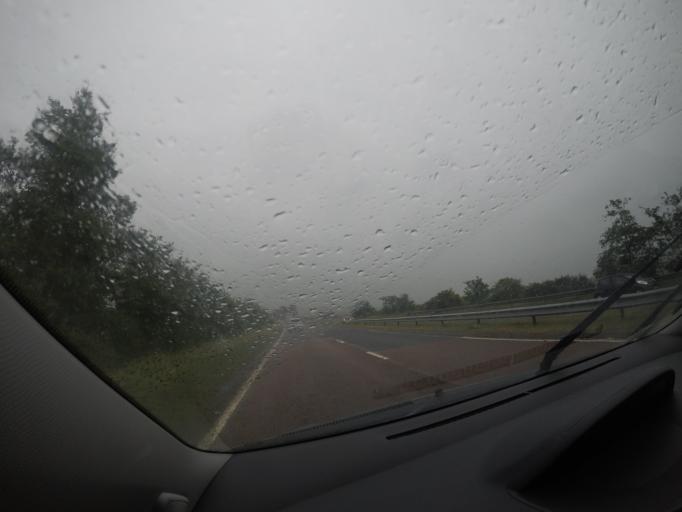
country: GB
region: Scotland
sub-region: Angus
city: Forfar
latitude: 56.6423
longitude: -2.9254
